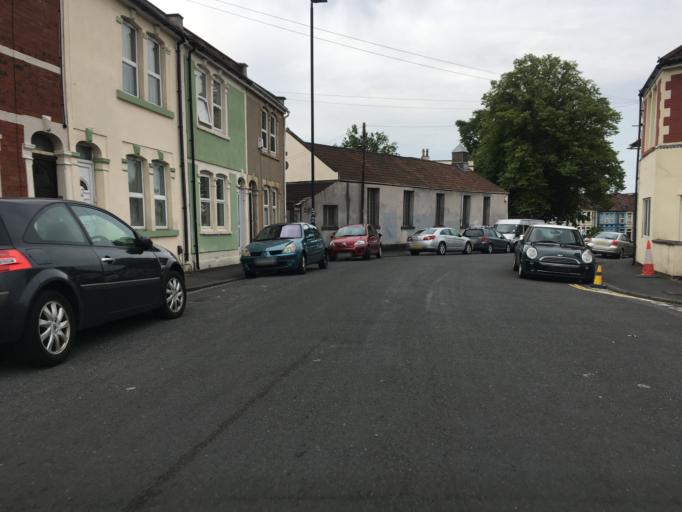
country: GB
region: England
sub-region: Bristol
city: Bristol
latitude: 51.4627
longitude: -2.5576
